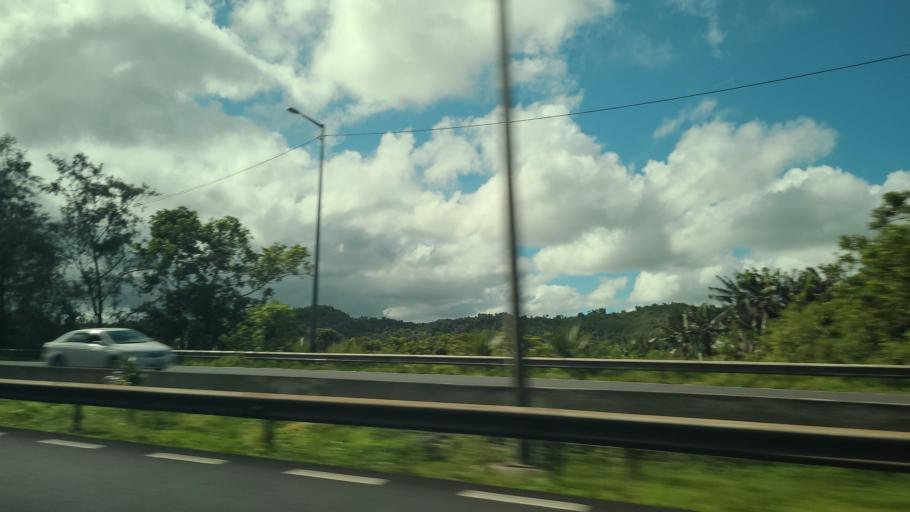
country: MU
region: Plaines Wilhems
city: Midlands
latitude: -20.3312
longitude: 57.5566
